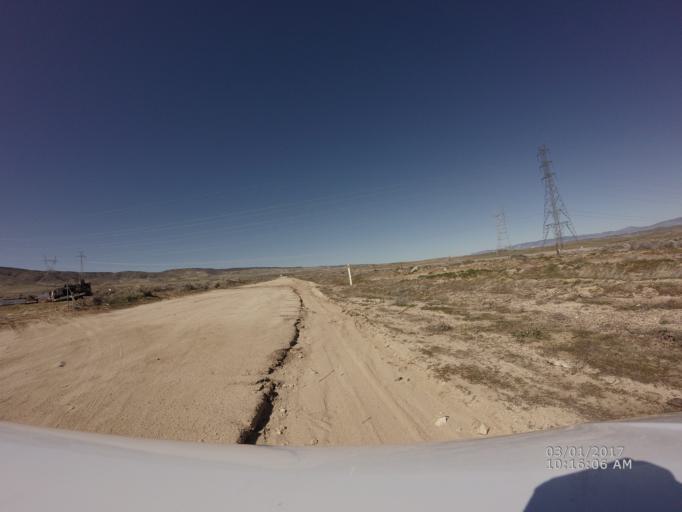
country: US
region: California
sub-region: Los Angeles County
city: Green Valley
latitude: 34.6892
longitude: -118.3546
